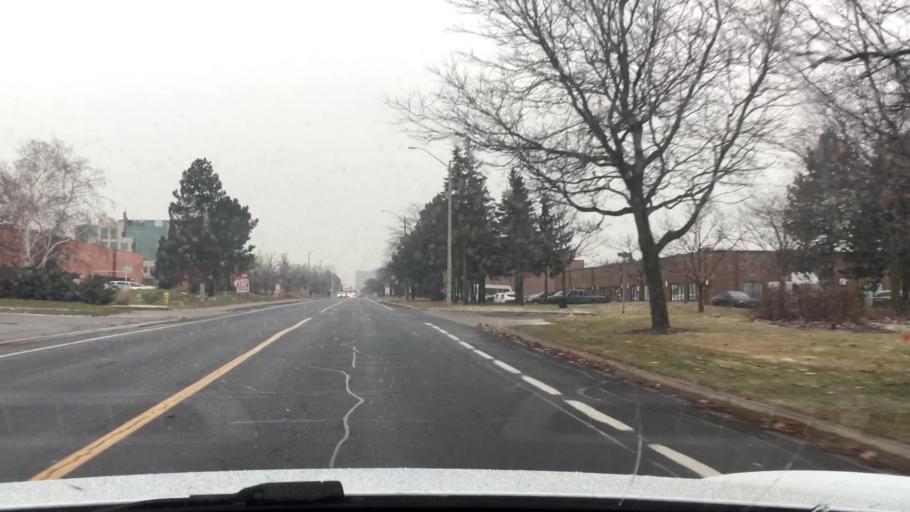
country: CA
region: Ontario
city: Markham
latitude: 43.8309
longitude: -79.3292
